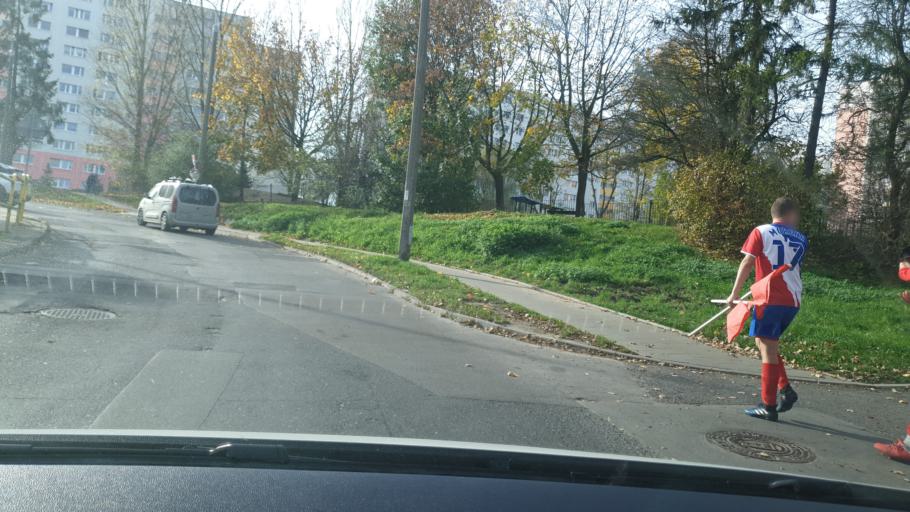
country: PL
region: Pomeranian Voivodeship
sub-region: Powiat gdanski
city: Kowale
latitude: 54.3610
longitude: 18.5809
